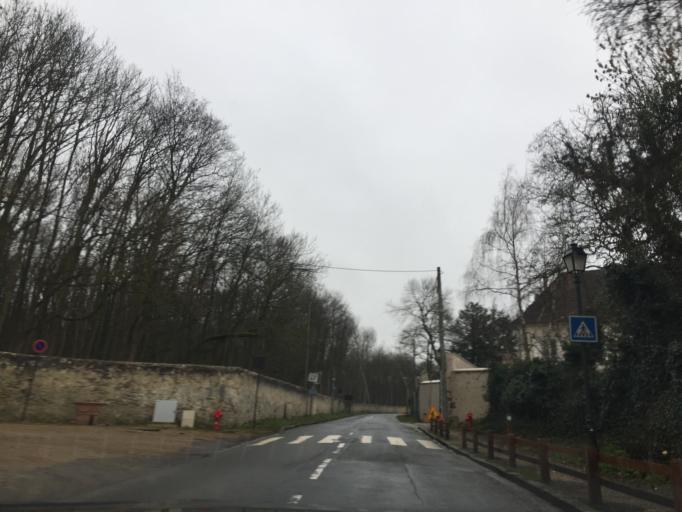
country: FR
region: Ile-de-France
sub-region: Departement de Seine-et-Marne
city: Coupvray
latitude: 48.8873
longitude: 2.7926
